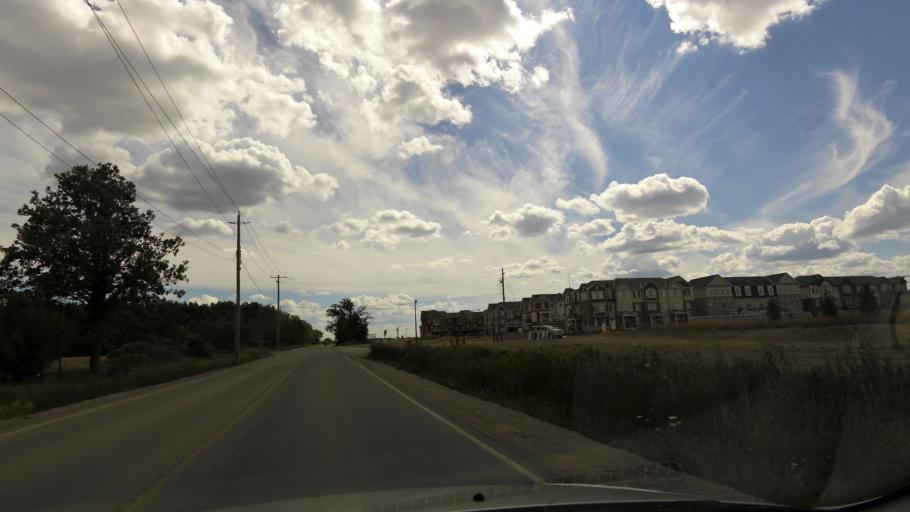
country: CA
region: Ontario
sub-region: Halton
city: Milton
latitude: 43.4844
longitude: -79.8372
